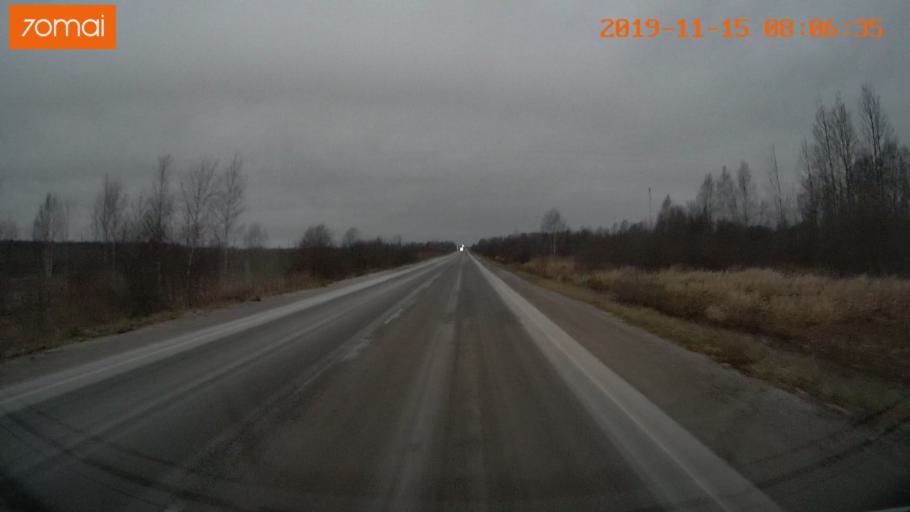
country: RU
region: Vologda
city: Cherepovets
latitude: 59.0228
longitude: 38.0352
